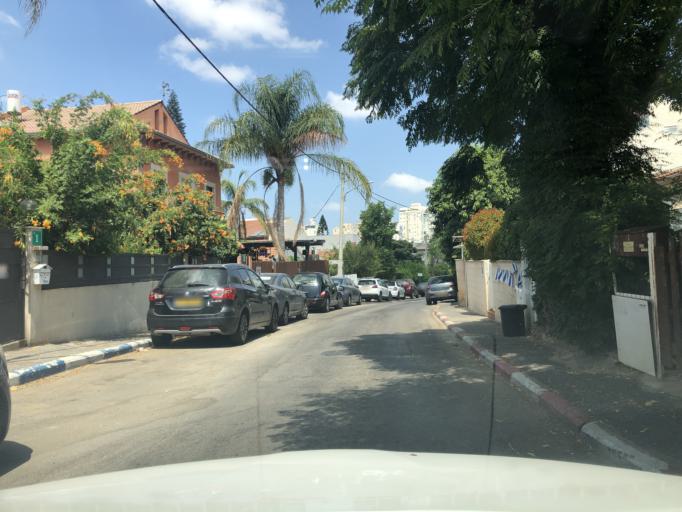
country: IL
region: Tel Aviv
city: Giv`at Shemu'el
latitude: 32.0654
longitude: 34.8491
